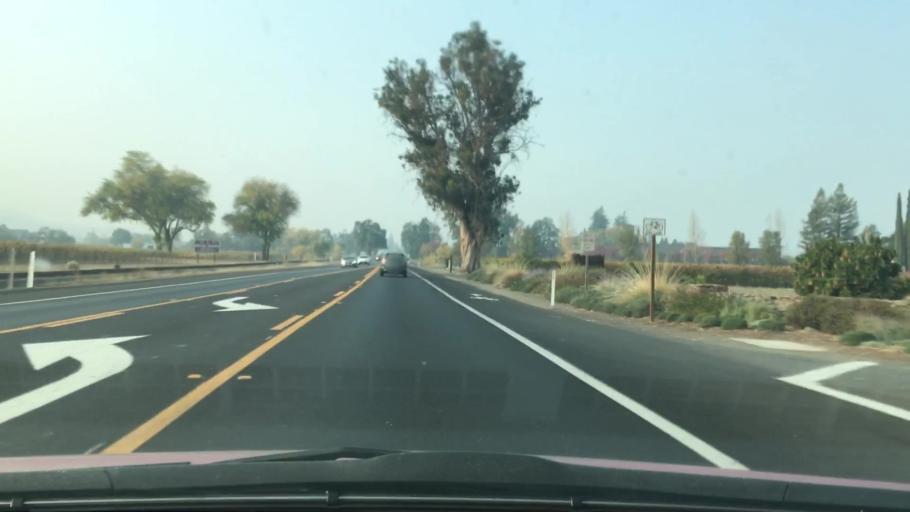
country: US
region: California
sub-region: Napa County
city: Yountville
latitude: 38.4441
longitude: -122.4093
